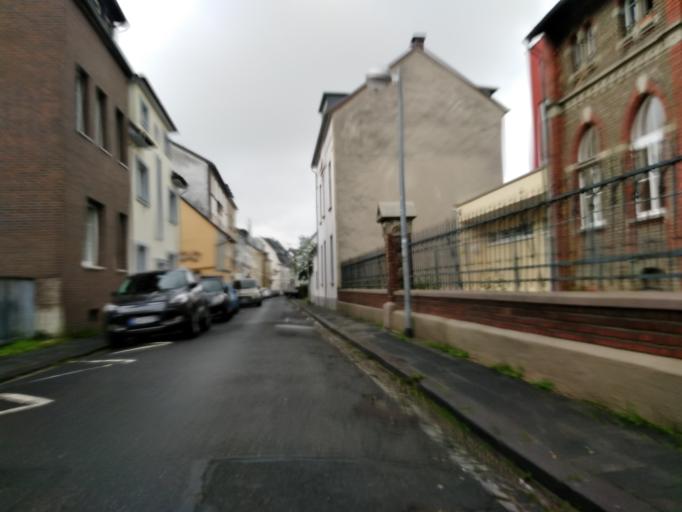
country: DE
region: North Rhine-Westphalia
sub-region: Regierungsbezirk Koln
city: Bad Honnef
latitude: 50.6476
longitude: 7.2273
